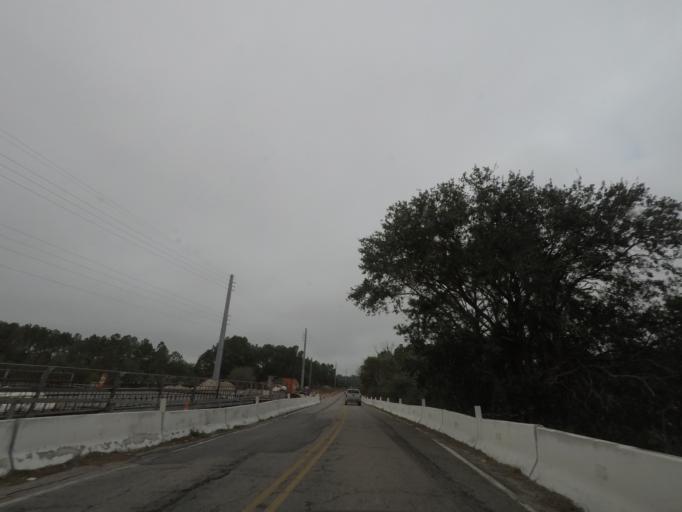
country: US
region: South Carolina
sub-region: Charleston County
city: Meggett
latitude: 32.5992
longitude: -80.3461
